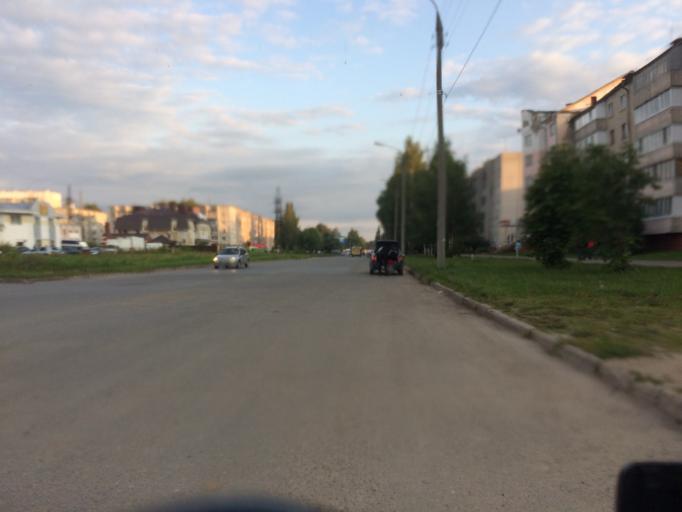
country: RU
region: Mariy-El
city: Medvedevo
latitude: 56.6445
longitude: 47.8446
